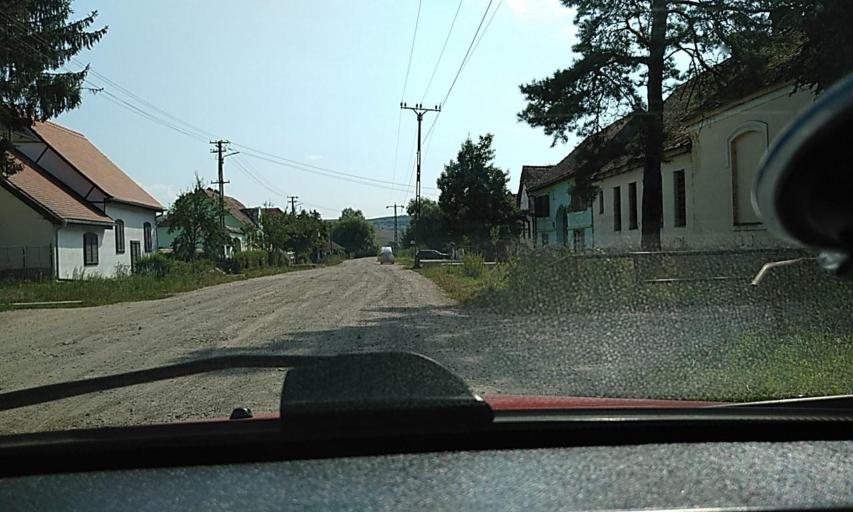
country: RO
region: Brasov
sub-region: Oras Rupea
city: Fiser
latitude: 46.0567
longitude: 25.0994
